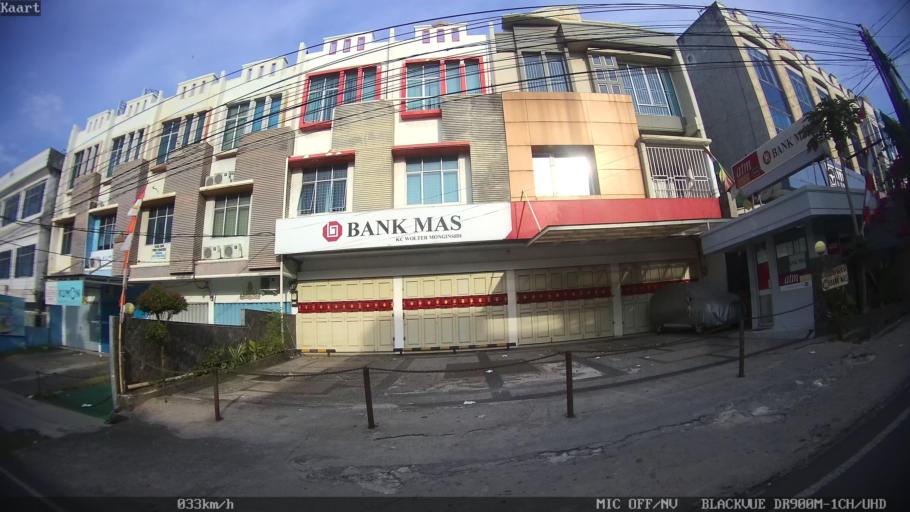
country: ID
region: Lampung
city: Bandarlampung
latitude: -5.4224
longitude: 105.2517
